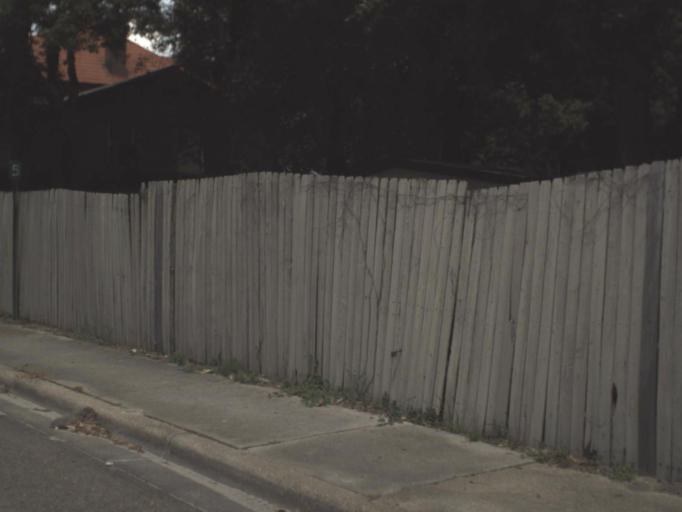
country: US
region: Florida
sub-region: Columbia County
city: Lake City
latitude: 30.1842
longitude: -82.6370
